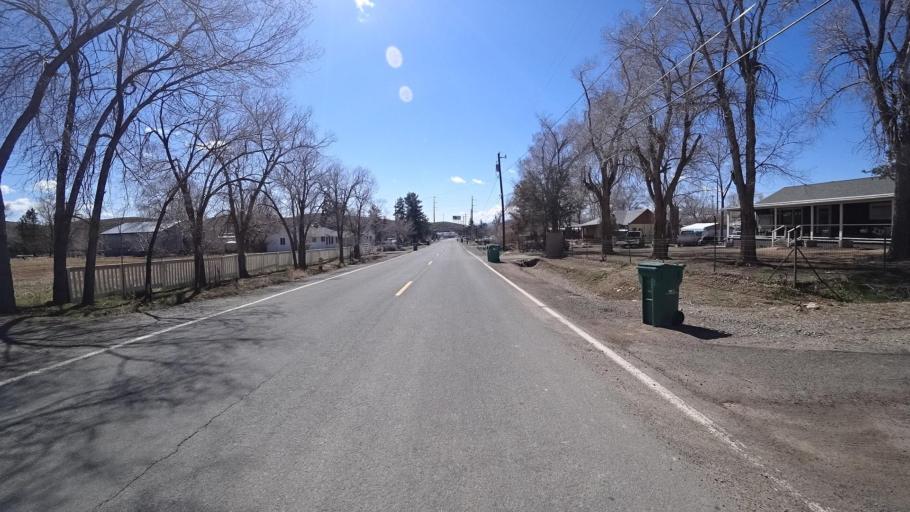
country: US
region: Nevada
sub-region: Washoe County
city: Golden Valley
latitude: 39.5911
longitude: -119.8228
